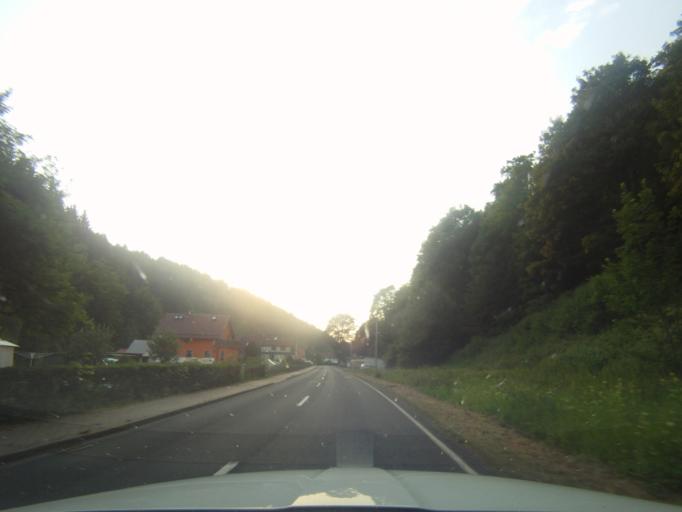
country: DE
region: Thuringia
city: Frauenwald
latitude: 50.4999
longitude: 10.8493
